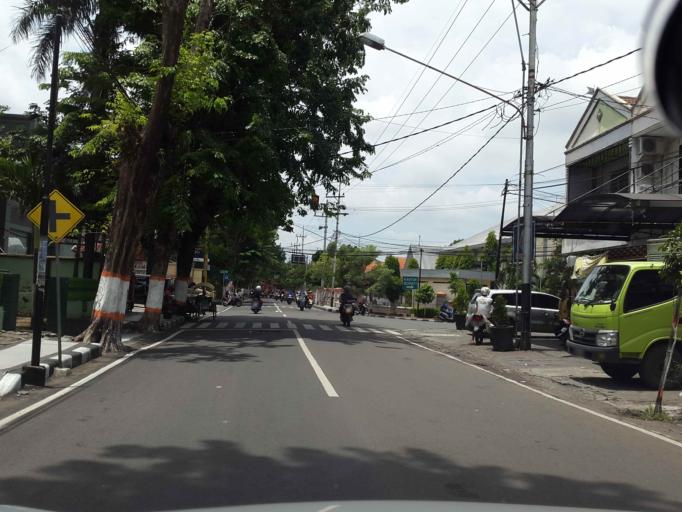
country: ID
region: East Java
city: Mojokerto
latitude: -7.4632
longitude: 112.4353
